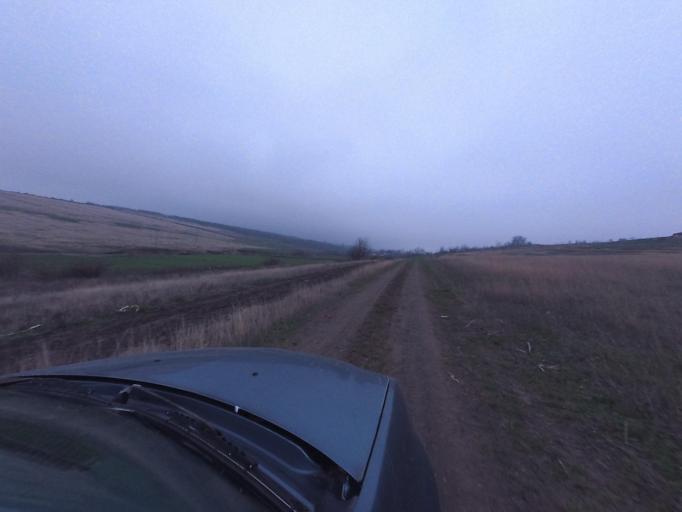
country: RO
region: Galati
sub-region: Comuna Balabanesti
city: Balabanesti
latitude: 46.1321
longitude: 27.7499
